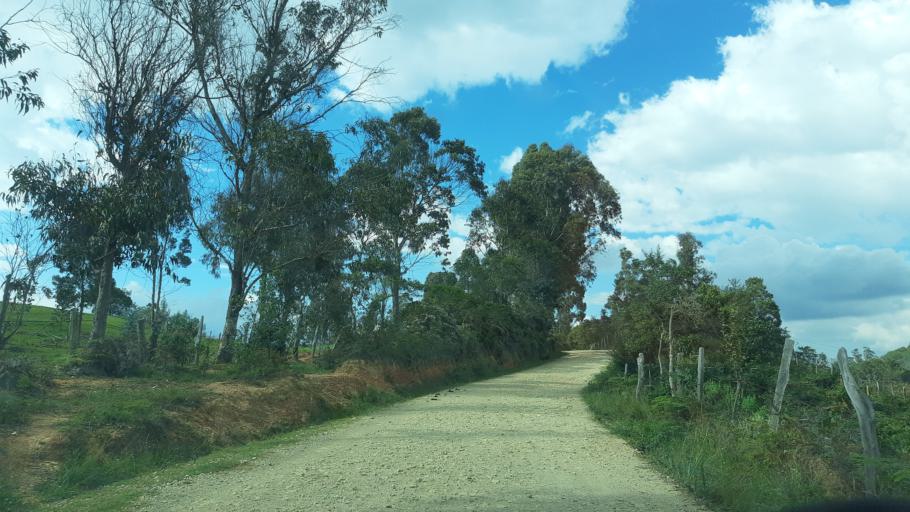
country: CO
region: Boyaca
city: Santa Sofia
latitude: 5.7402
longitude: -73.5523
